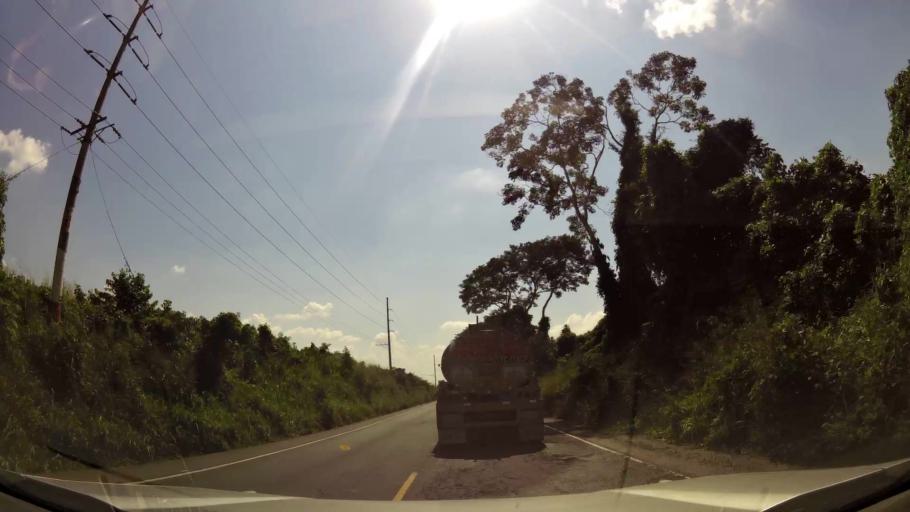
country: GT
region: Suchitepeque
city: Mazatenango
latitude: 14.5441
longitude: -91.5219
